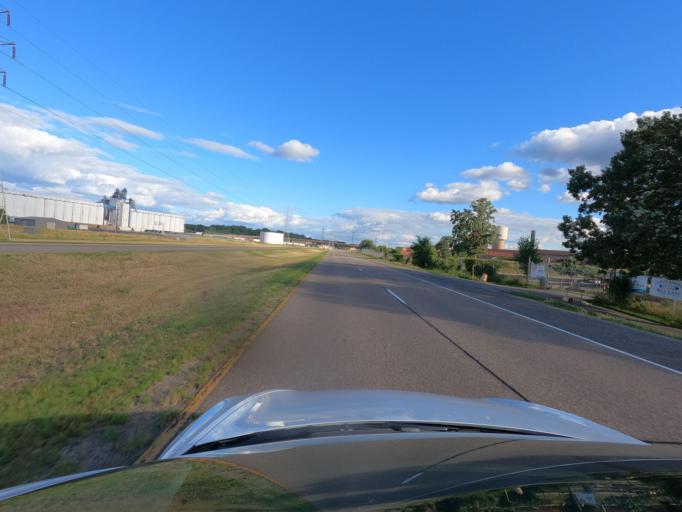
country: US
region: Minnesota
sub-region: Anoka County
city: Columbia Heights
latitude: 45.0510
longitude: -93.2769
